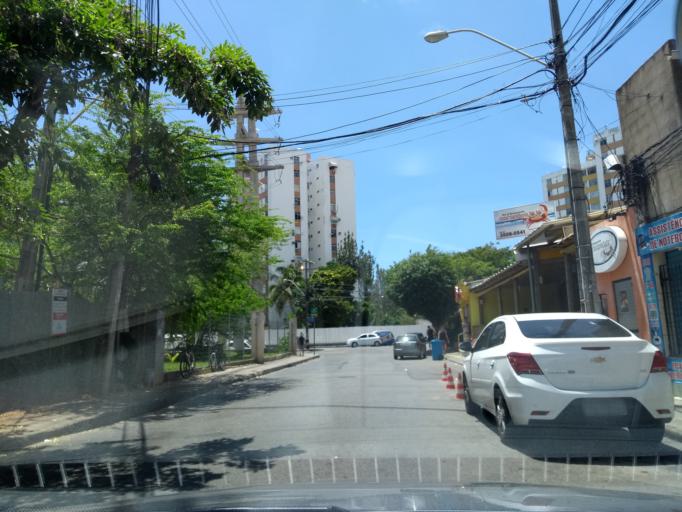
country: BR
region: Bahia
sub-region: Salvador
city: Salvador
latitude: -12.9651
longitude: -38.4326
